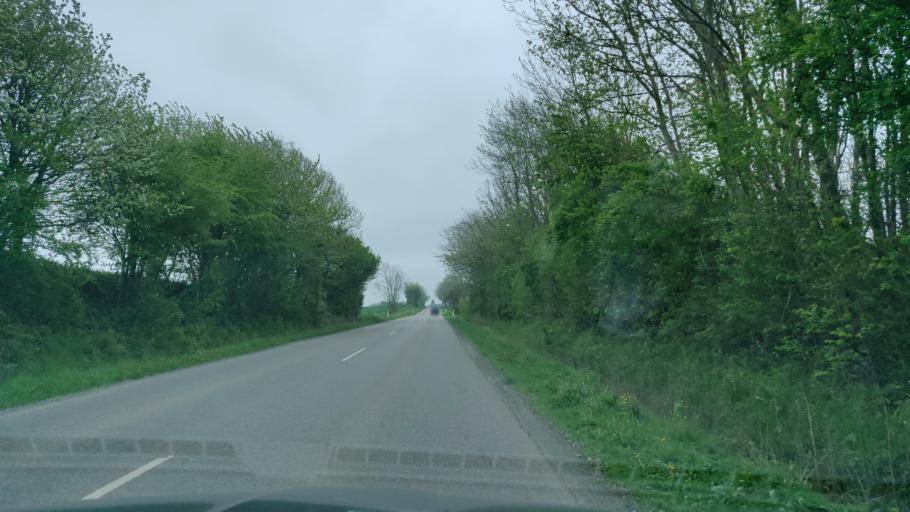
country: DK
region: South Denmark
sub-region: Sonderborg Kommune
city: Guderup
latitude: 54.9961
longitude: 9.9567
